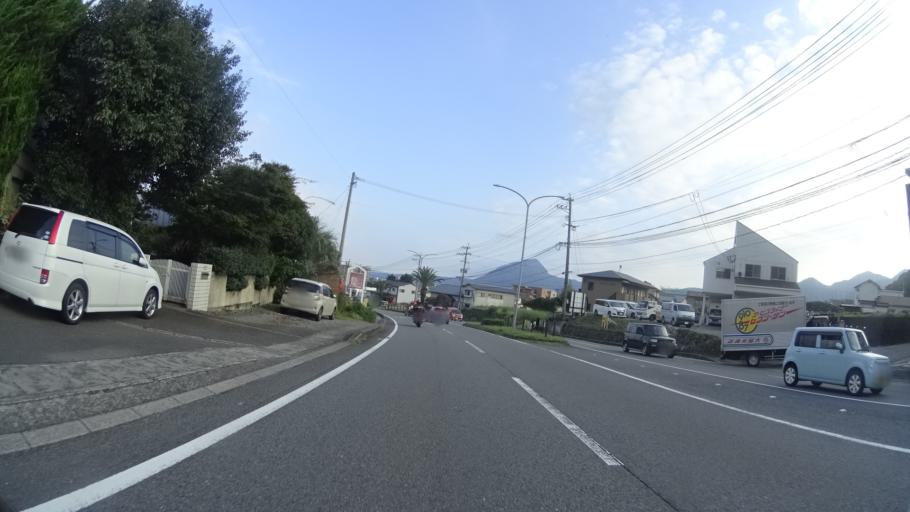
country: JP
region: Oita
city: Beppu
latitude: 33.3062
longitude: 131.4891
